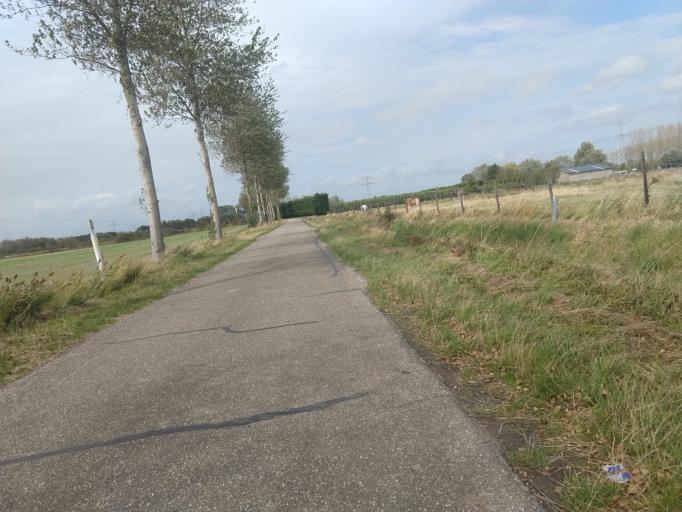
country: NL
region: Zeeland
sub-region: Gemeente Reimerswaal
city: Yerseke
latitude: 51.4543
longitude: 3.9988
